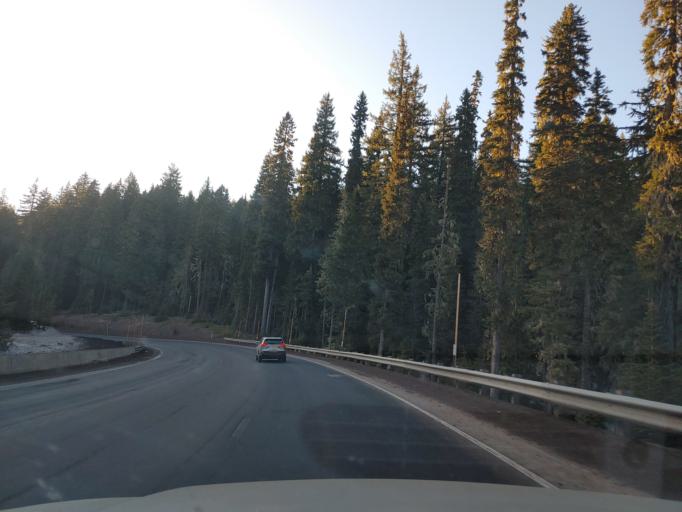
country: US
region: Oregon
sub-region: Lane County
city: Oakridge
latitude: 43.6202
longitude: -122.0679
